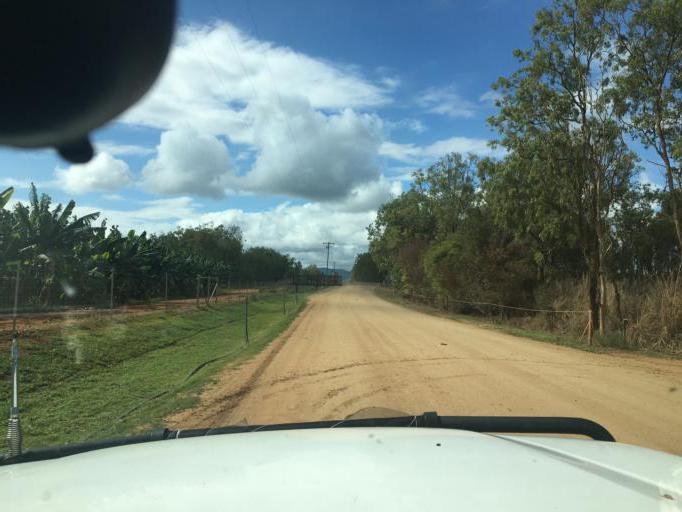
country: AU
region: Queensland
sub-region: Tablelands
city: Mareeba
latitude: -17.0977
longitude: 145.4120
